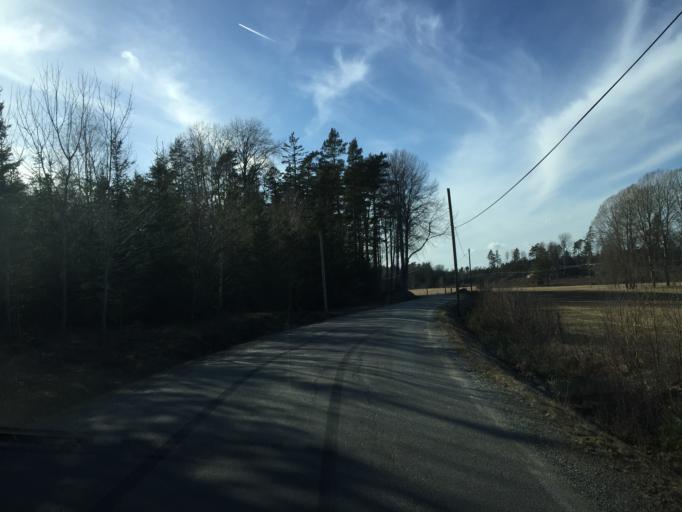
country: SE
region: Stockholm
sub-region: Nynashamns Kommun
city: Osmo
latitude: 59.0461
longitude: 17.8351
